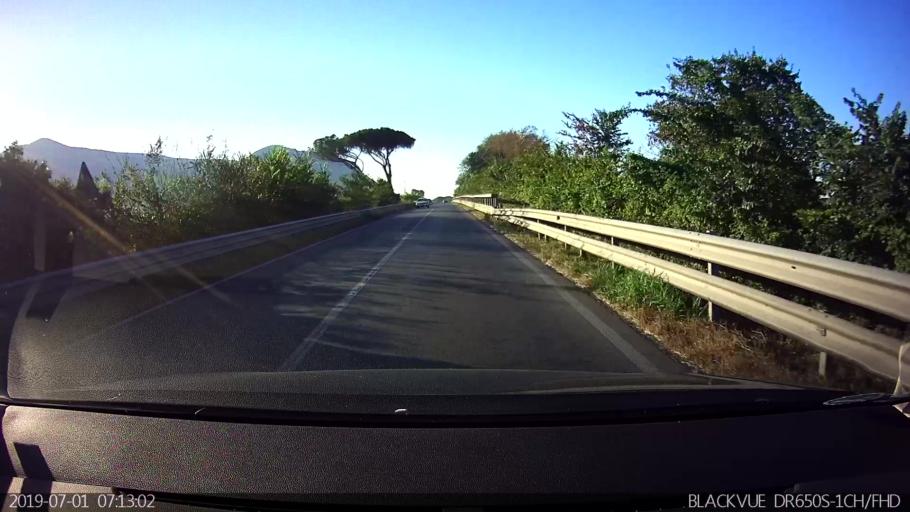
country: IT
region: Latium
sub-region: Provincia di Latina
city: Borgo Hermada
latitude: 41.3303
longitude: 13.1727
